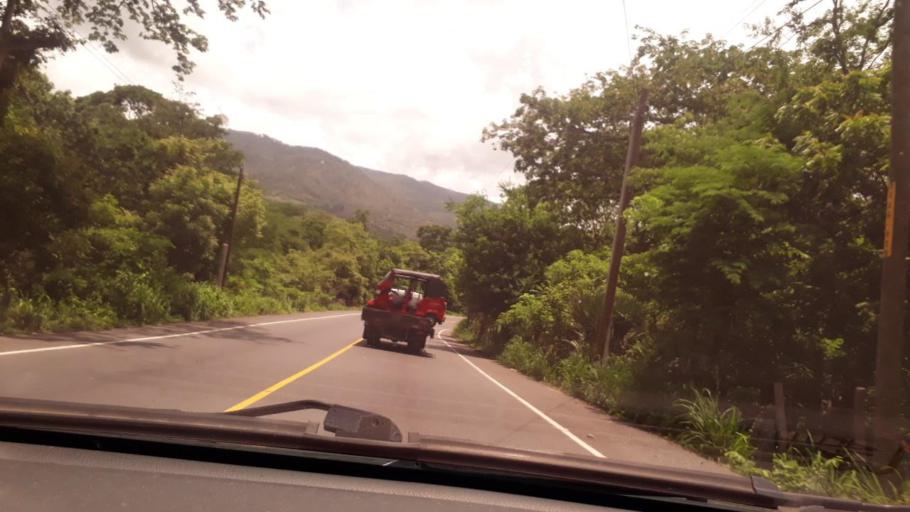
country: GT
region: Zacapa
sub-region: Municipio de Zacapa
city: Gualan
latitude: 15.1367
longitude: -89.3389
